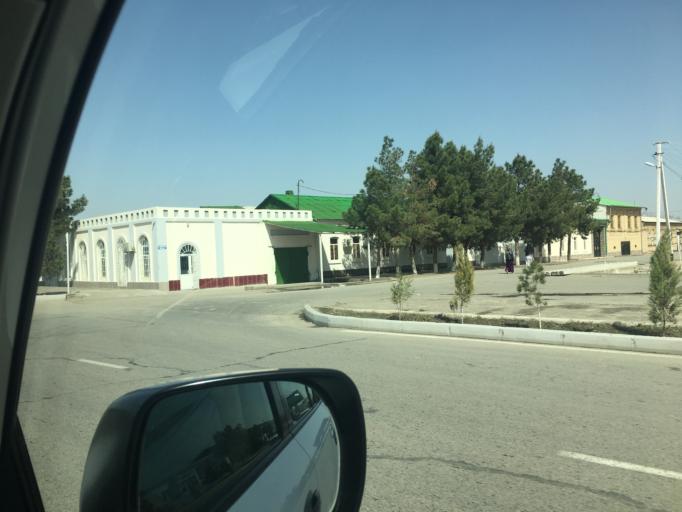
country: TM
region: Lebap
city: Turkmenabat
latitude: 39.0246
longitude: 63.5970
